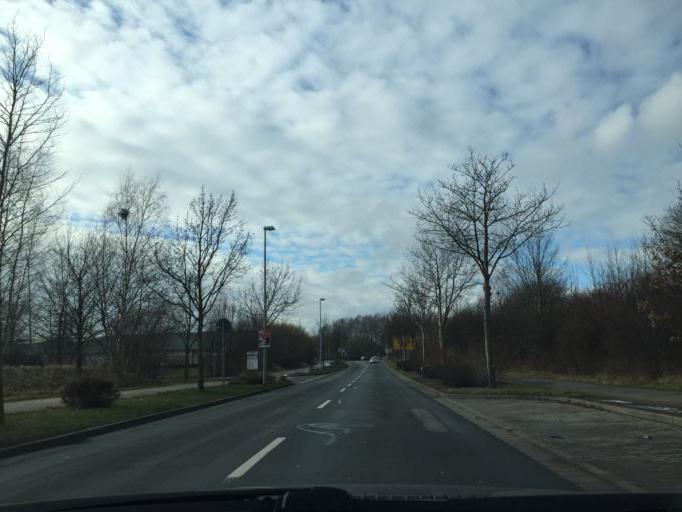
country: DE
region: Saxony
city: Radeberg
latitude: 51.1310
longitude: 13.9206
